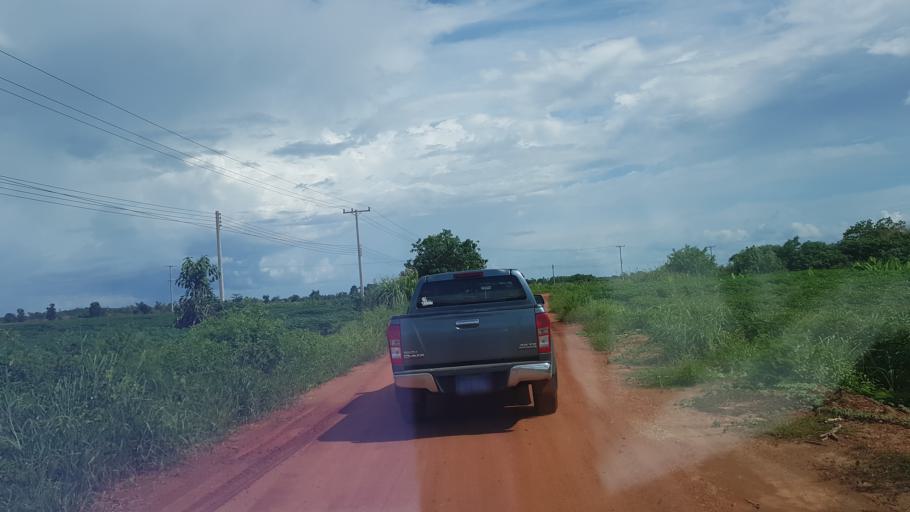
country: LA
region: Vientiane
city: Vientiane
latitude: 18.2197
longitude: 102.5691
